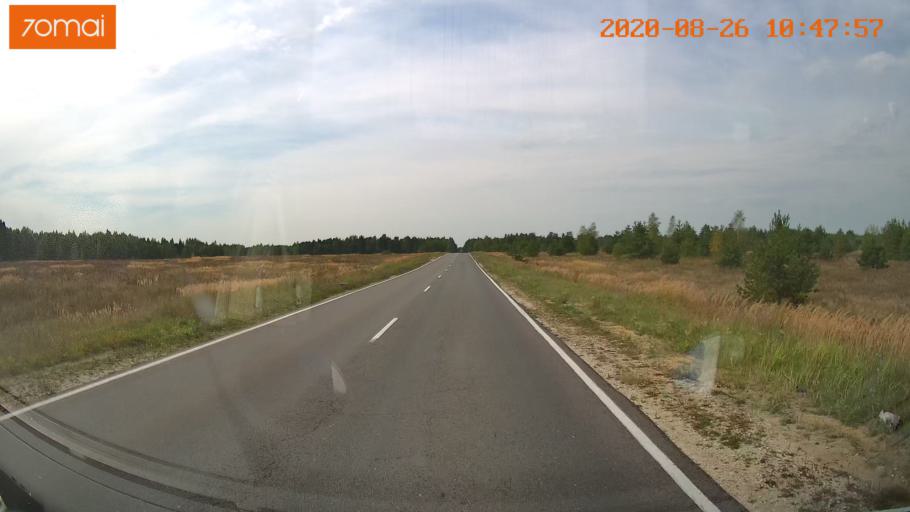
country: RU
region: Rjazan
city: Lashma
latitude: 54.7207
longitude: 41.1818
